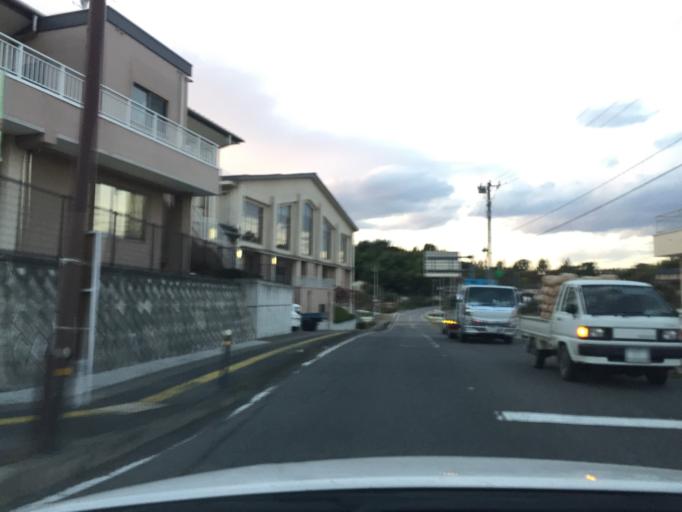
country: JP
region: Fukushima
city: Miharu
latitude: 37.4555
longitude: 140.4405
